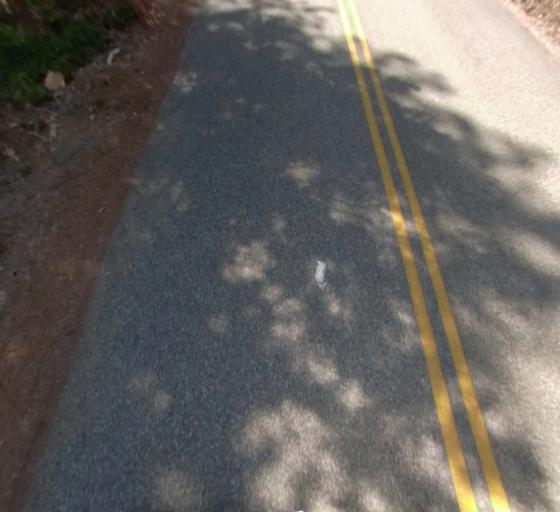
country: US
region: California
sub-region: Madera County
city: Oakhurst
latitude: 37.3432
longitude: -119.3811
